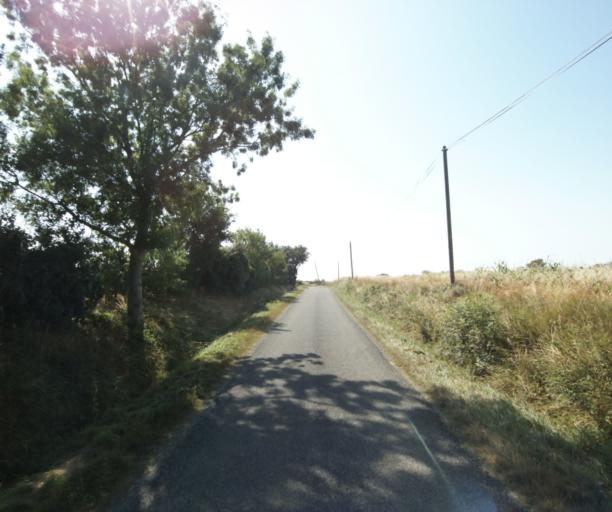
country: FR
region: Midi-Pyrenees
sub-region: Departement de la Haute-Garonne
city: Saint-Felix-Lauragais
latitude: 43.4285
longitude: 1.8251
